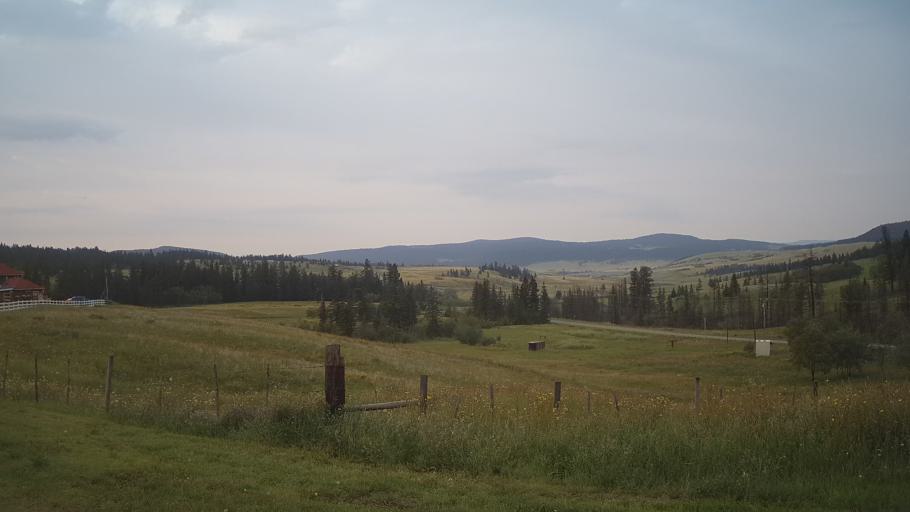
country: CA
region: British Columbia
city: Williams Lake
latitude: 51.9692
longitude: -122.5308
